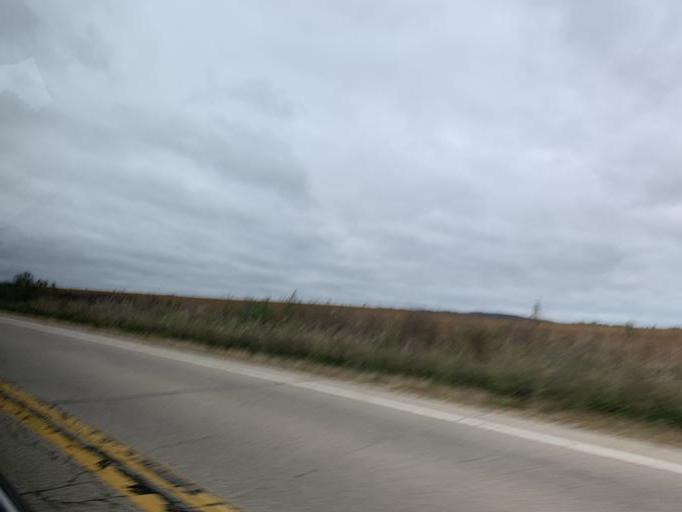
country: US
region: Wisconsin
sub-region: Grant County
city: Muscoda
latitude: 43.2118
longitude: -90.5617
